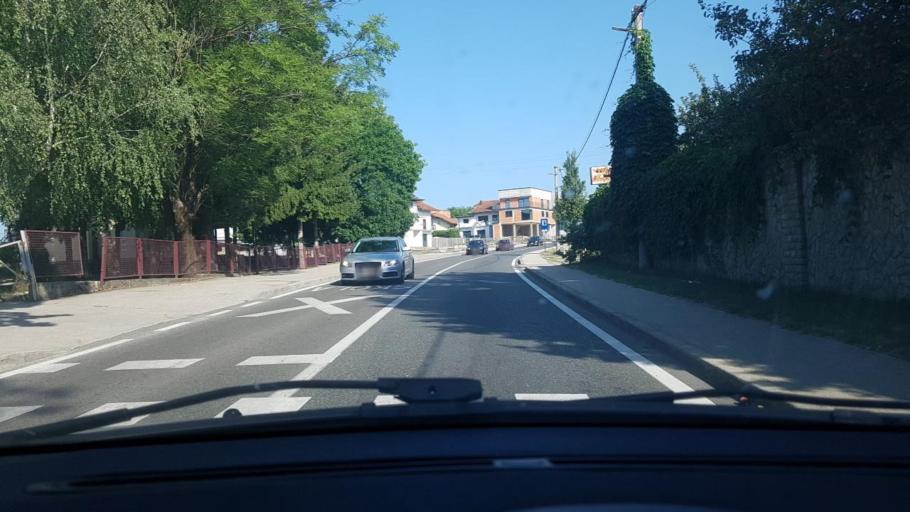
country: BA
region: Federation of Bosnia and Herzegovina
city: Ostrozac
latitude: 44.9085
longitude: 15.9326
